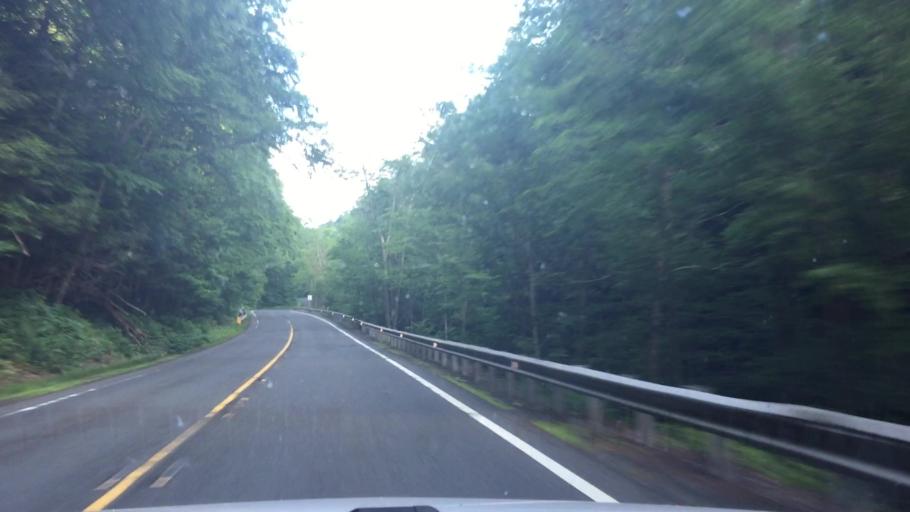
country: US
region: Massachusetts
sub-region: Hampshire County
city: Chesterfield
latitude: 42.3278
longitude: -72.8739
